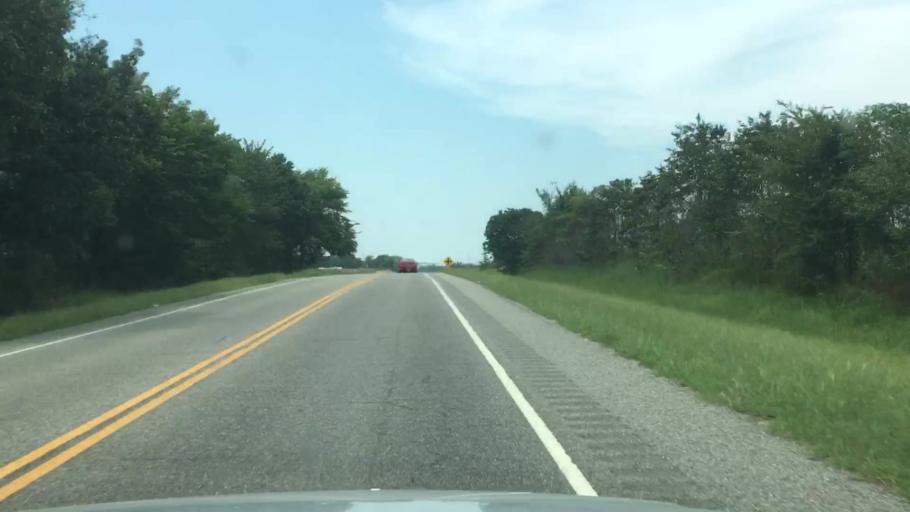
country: US
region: Oklahoma
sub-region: Muskogee County
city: Fort Gibson
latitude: 35.9369
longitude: -95.1665
